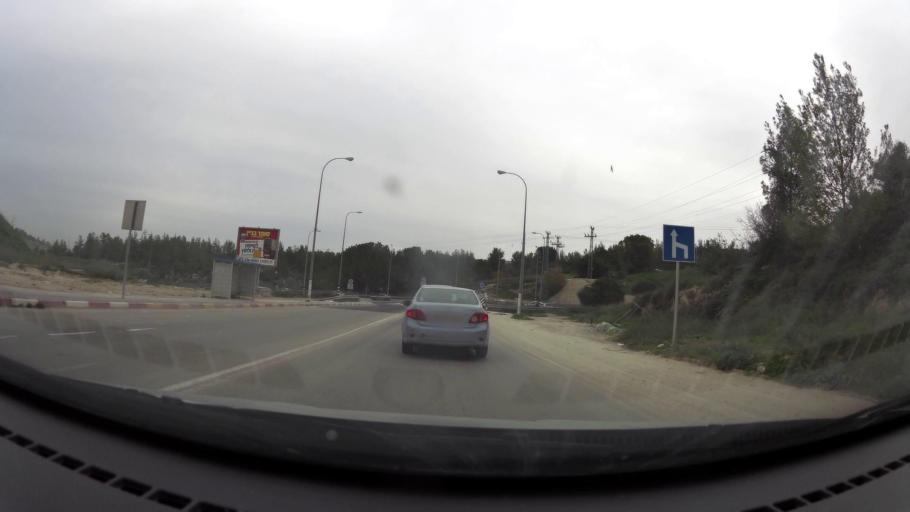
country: IL
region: Jerusalem
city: Bet Shemesh
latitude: 31.7048
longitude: 35.0083
